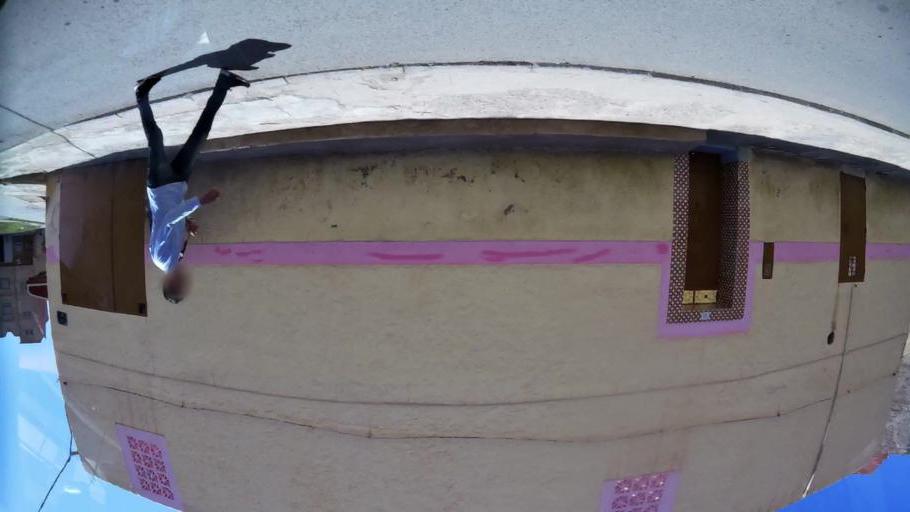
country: MA
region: Oriental
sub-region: Oujda-Angad
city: Oujda
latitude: 34.6899
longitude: -1.9294
